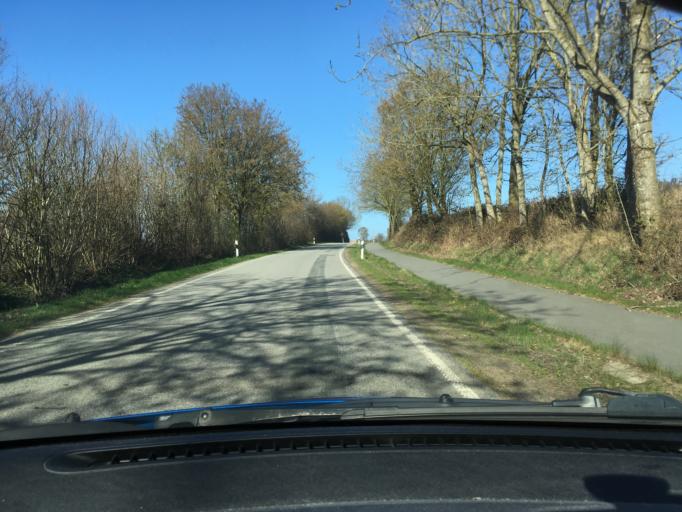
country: DE
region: Schleswig-Holstein
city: Fahrdorf
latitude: 54.5031
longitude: 9.6314
